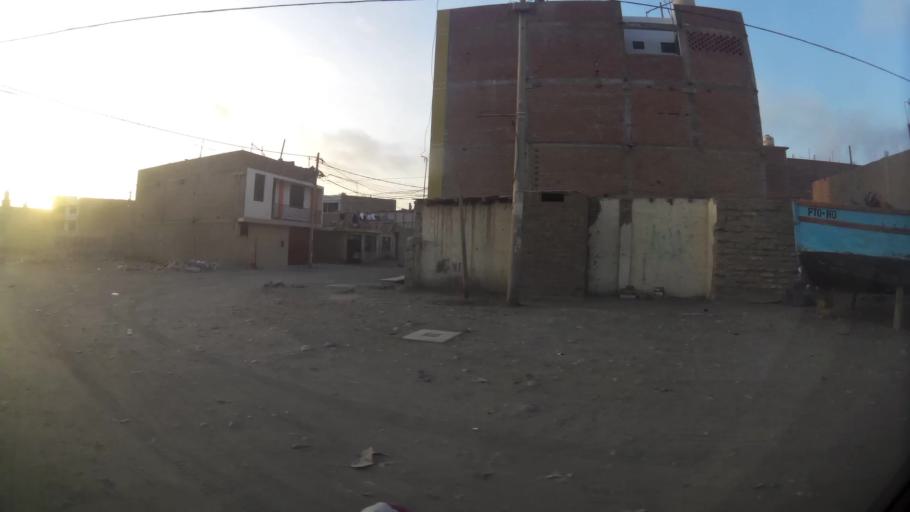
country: PE
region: Lima
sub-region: Huaura
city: Huacho
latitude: -11.1195
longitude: -77.6085
